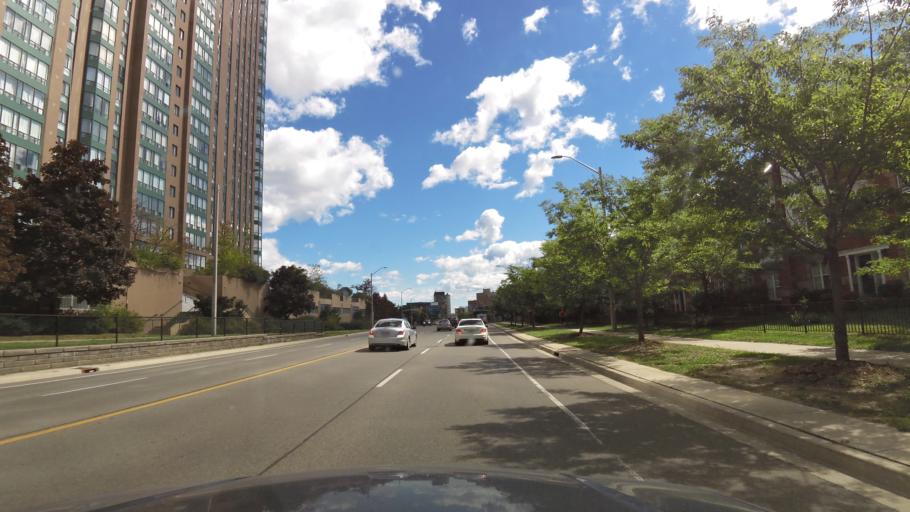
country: CA
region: Ontario
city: Mississauga
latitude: 43.5802
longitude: -79.6258
